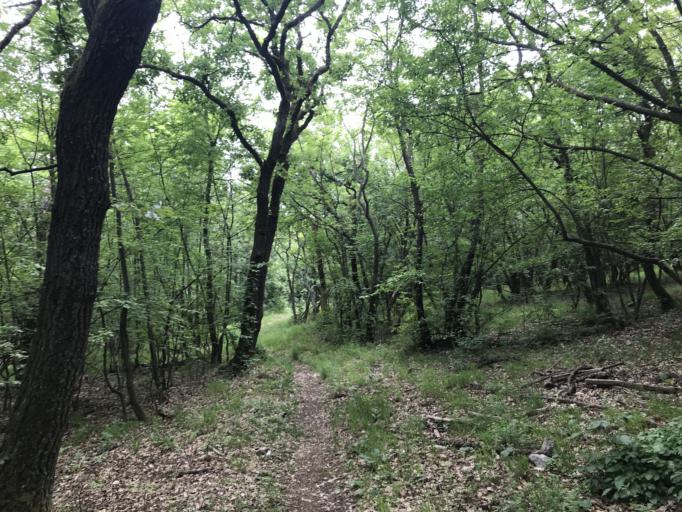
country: HU
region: Pest
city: Csobanka
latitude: 47.6592
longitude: 18.9344
